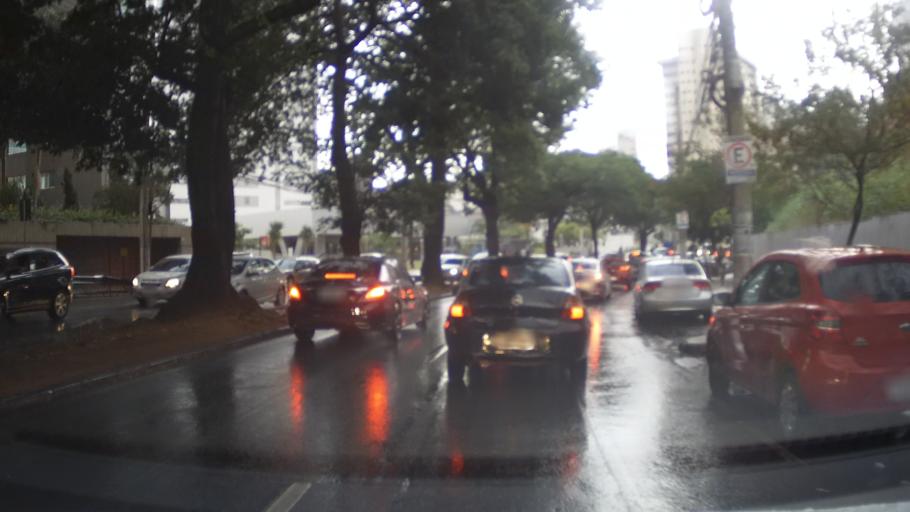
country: BR
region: Minas Gerais
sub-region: Belo Horizonte
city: Belo Horizonte
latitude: -19.9447
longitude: -43.9568
